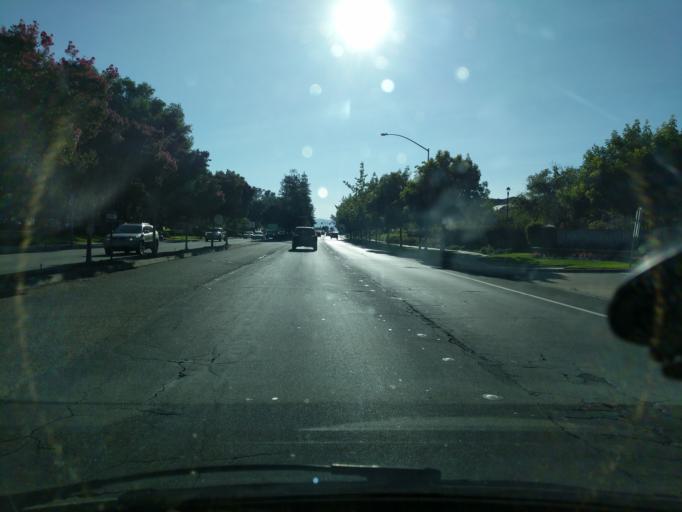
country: US
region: California
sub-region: Alameda County
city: Livermore
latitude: 37.6785
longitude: -121.7845
